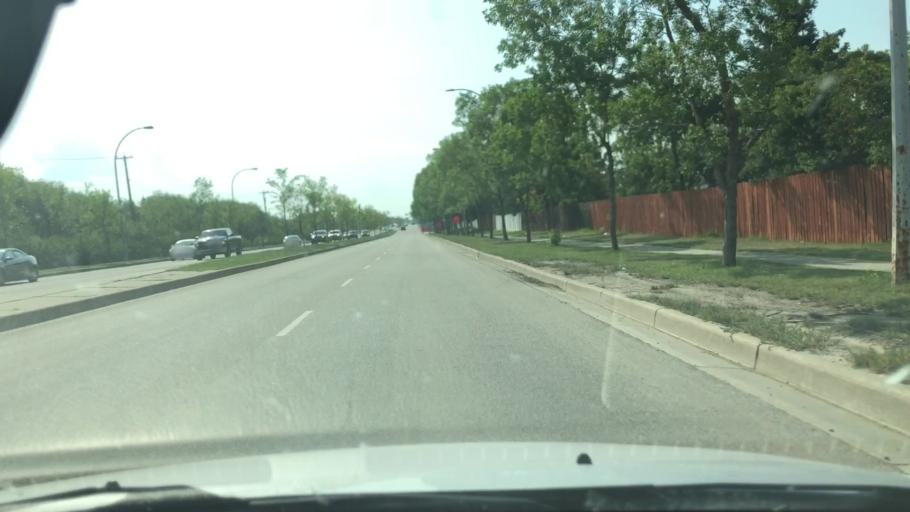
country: CA
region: Alberta
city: Edmonton
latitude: 53.6141
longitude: -113.4977
